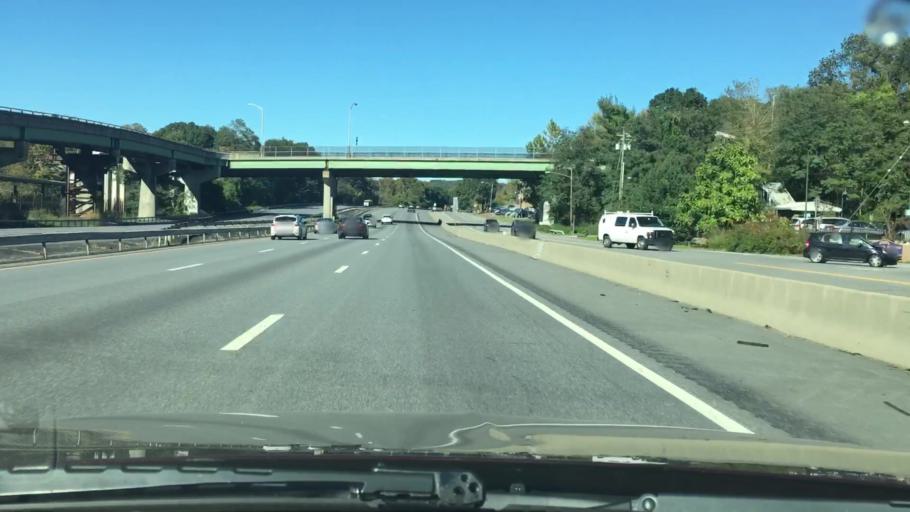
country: US
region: New York
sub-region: Westchester County
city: Goldens Bridge
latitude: 41.2939
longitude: -73.6770
